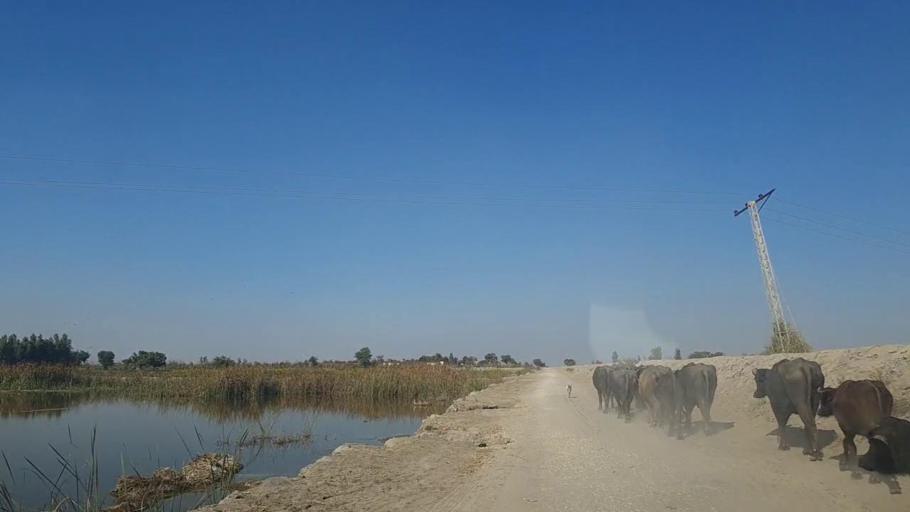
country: PK
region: Sindh
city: Sanghar
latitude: 26.2181
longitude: 68.9291
